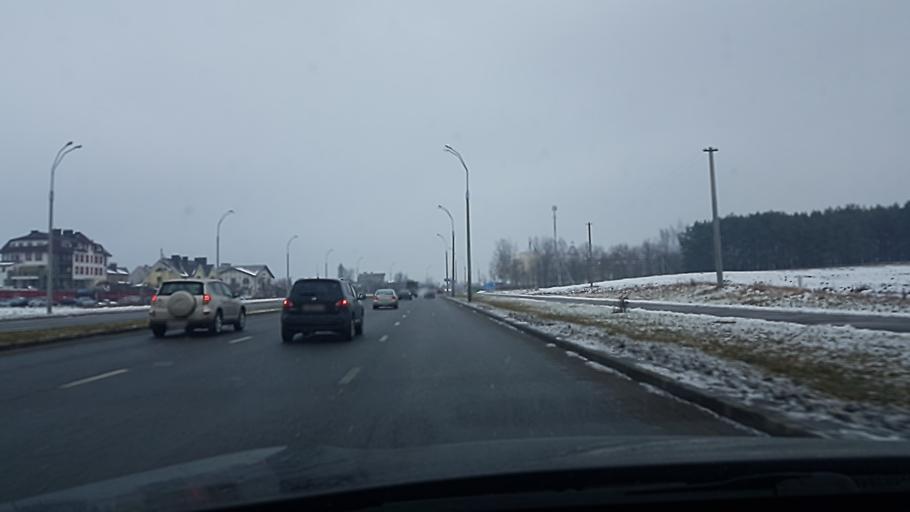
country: BY
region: Minsk
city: Minsk
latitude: 53.9504
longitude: 27.5358
